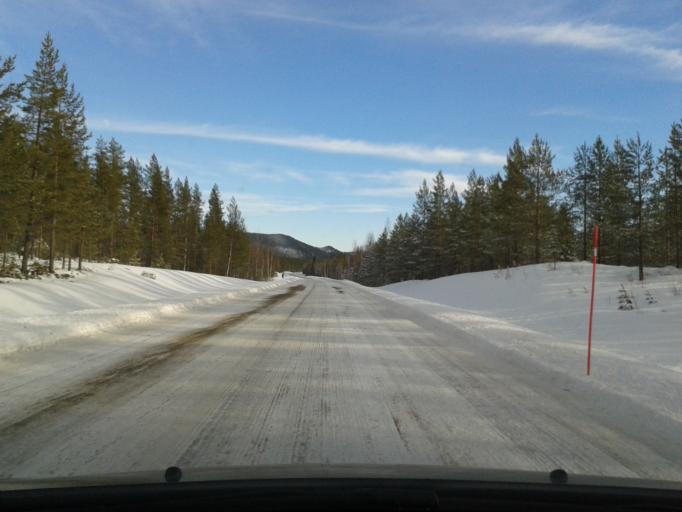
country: SE
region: Vaesterbotten
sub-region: Asele Kommun
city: Asele
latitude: 64.3165
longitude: 17.1437
